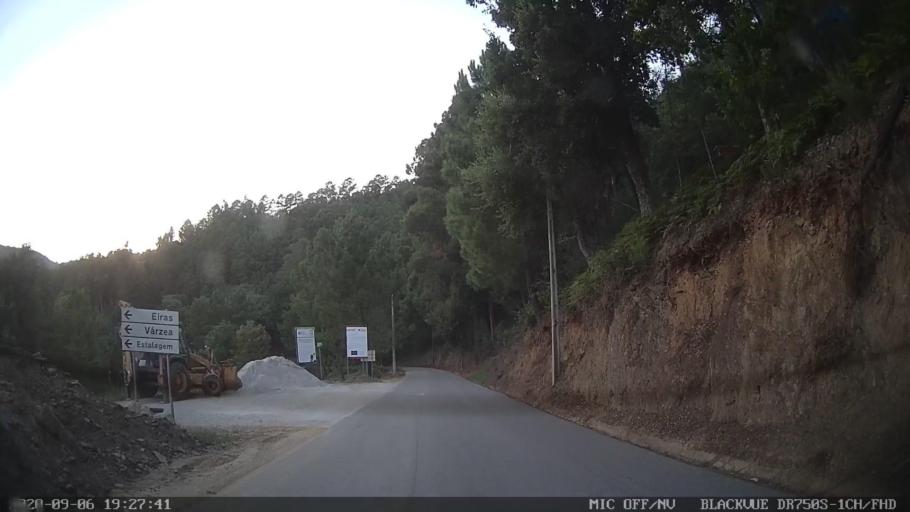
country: PT
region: Vila Real
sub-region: Mesao Frio
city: Mesao Frio
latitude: 41.1809
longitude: -7.9089
